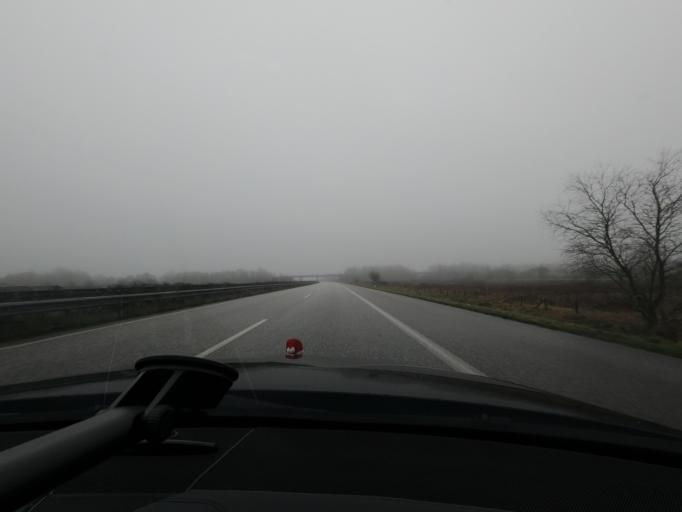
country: DE
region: Schleswig-Holstein
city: Sankelmark
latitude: 54.7055
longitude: 9.4016
